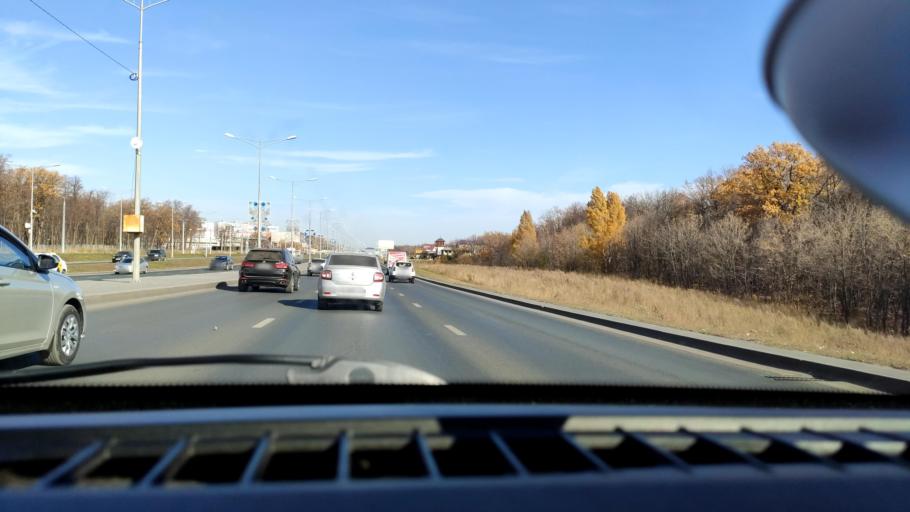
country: RU
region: Samara
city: Petra-Dubrava
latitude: 53.2672
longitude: 50.2509
